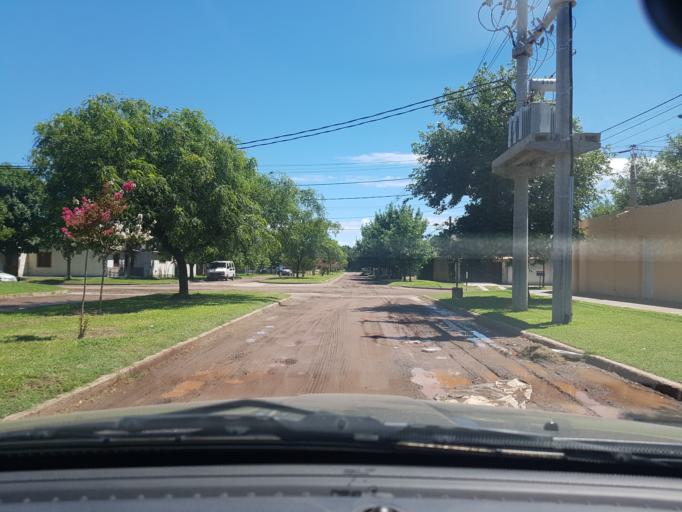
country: AR
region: Cordoba
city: Las Perdices
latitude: -32.7584
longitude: -63.7751
